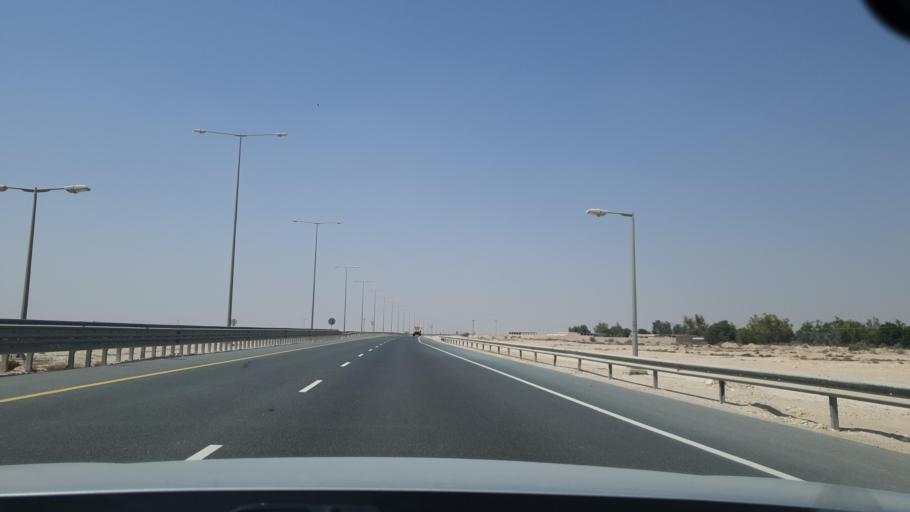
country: QA
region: Baladiyat az Za`ayin
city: Az Za`ayin
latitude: 25.6189
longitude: 51.3547
